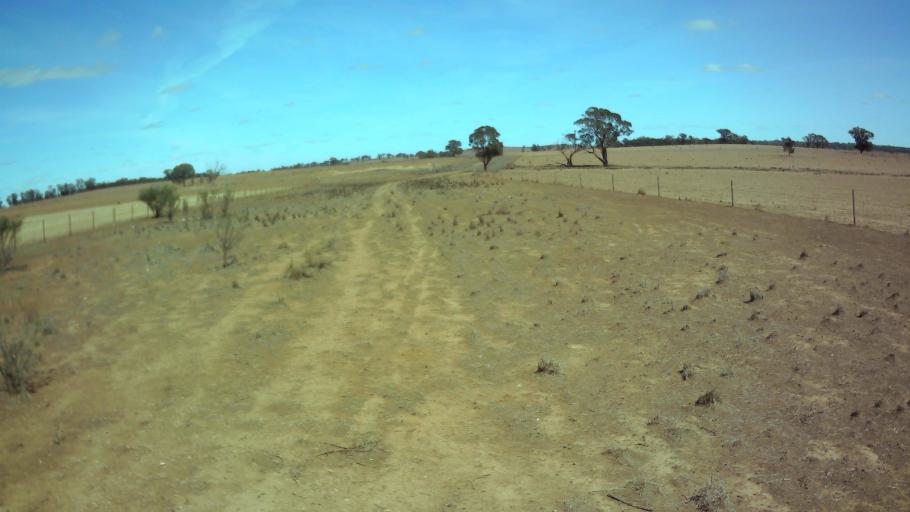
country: AU
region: New South Wales
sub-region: Weddin
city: Grenfell
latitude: -33.7247
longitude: 147.8651
